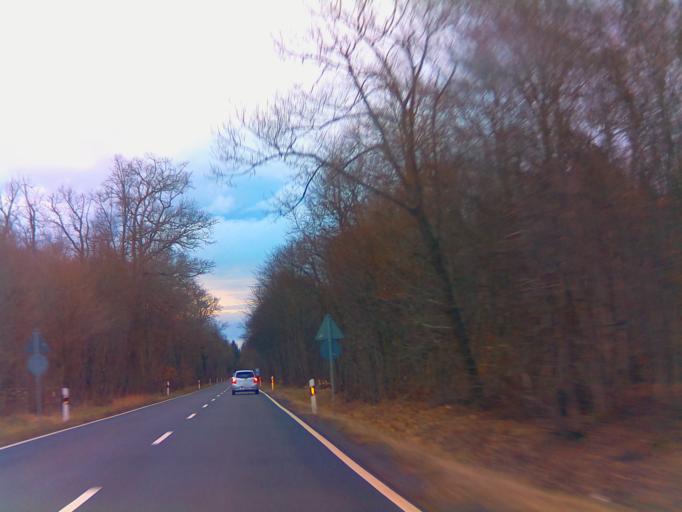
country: DE
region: Hesse
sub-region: Regierungsbezirk Darmstadt
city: Einhausen
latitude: 49.6988
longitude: 8.5180
